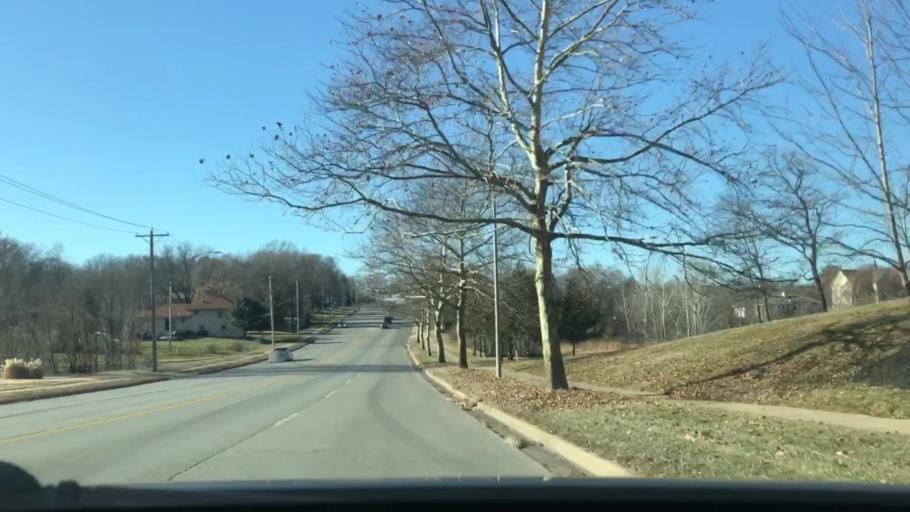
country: US
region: Missouri
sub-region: Jackson County
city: East Independence
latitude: 39.0488
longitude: -94.3810
